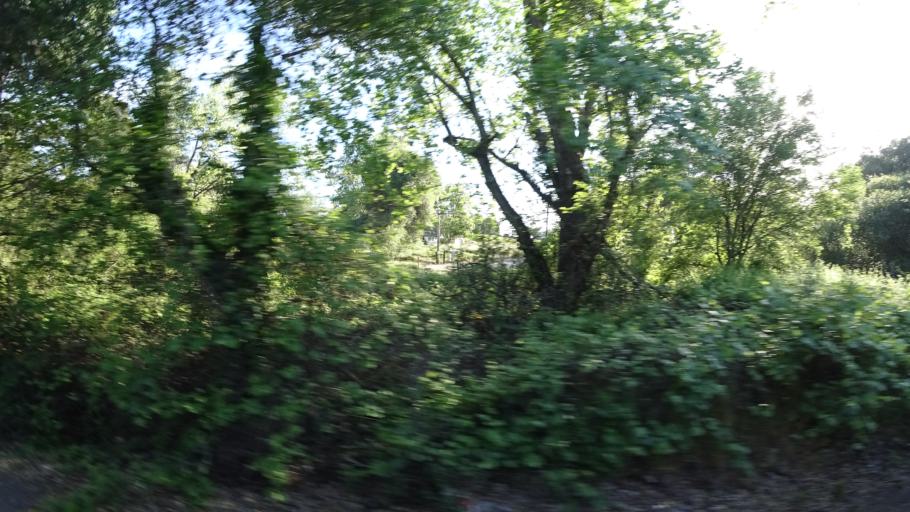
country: US
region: California
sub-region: Placer County
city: Lincoln
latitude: 38.9233
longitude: -121.2282
